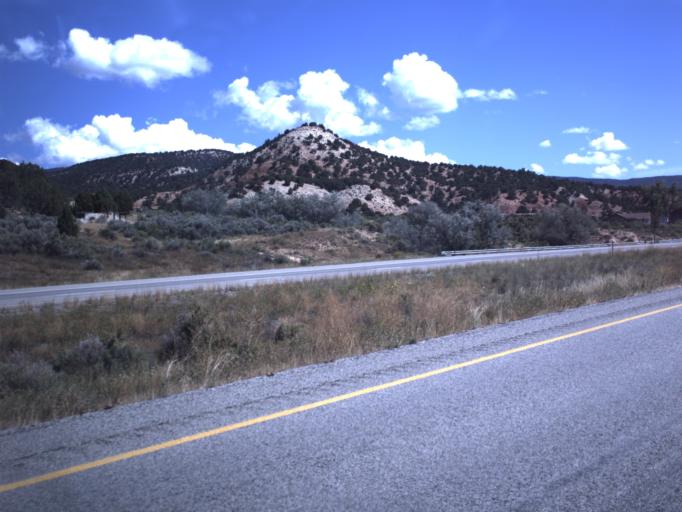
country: US
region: Utah
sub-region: Sevier County
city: Salina
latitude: 38.9205
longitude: -111.7566
